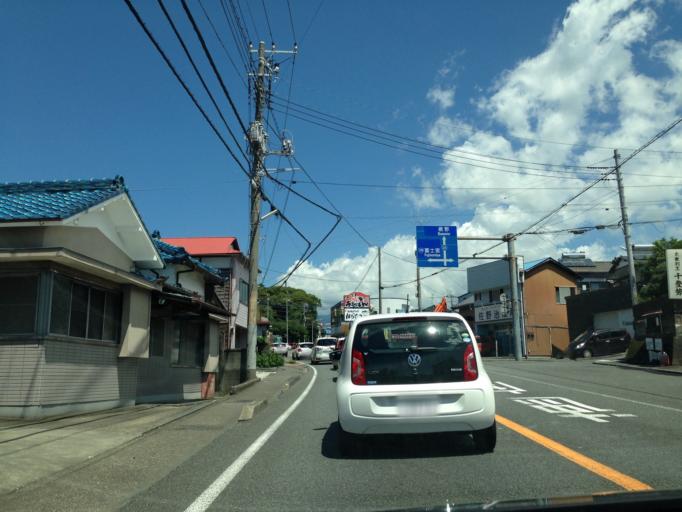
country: JP
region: Shizuoka
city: Fuji
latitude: 35.1682
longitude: 138.6892
